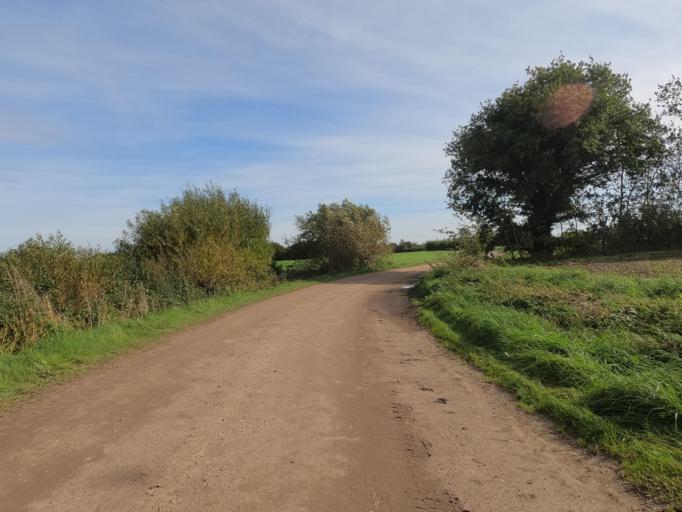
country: DE
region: Schleswig-Holstein
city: Riepsdorf
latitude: 54.2321
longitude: 10.9826
